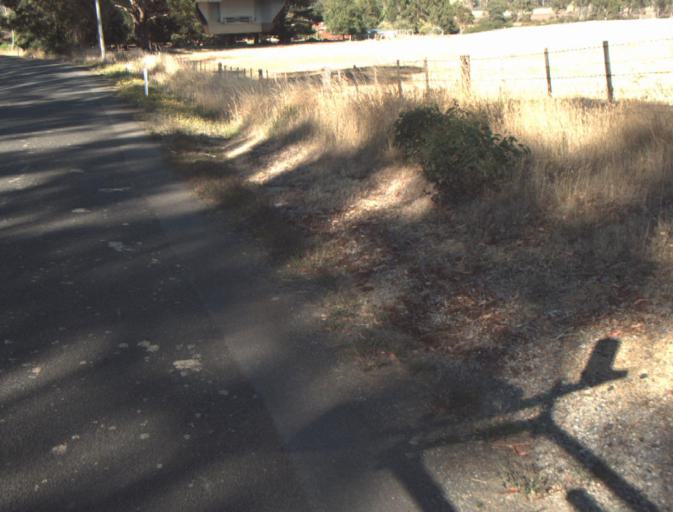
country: AU
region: Tasmania
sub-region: Launceston
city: Newstead
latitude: -41.3370
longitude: 147.3048
